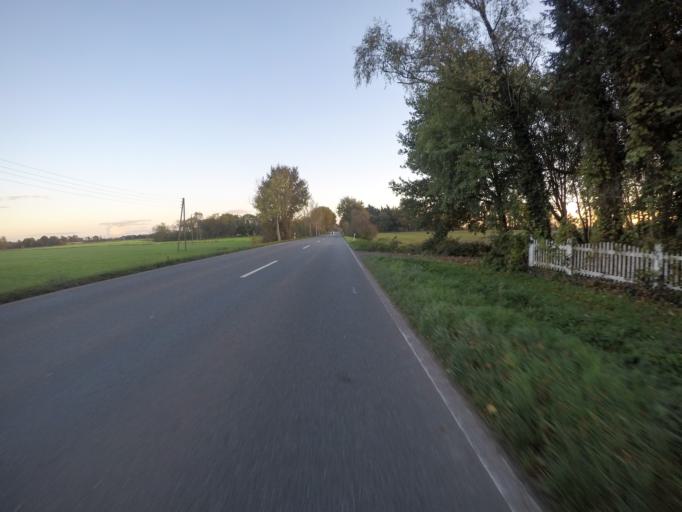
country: DE
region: North Rhine-Westphalia
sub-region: Regierungsbezirk Munster
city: Isselburg
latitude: 51.8504
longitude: 6.4750
